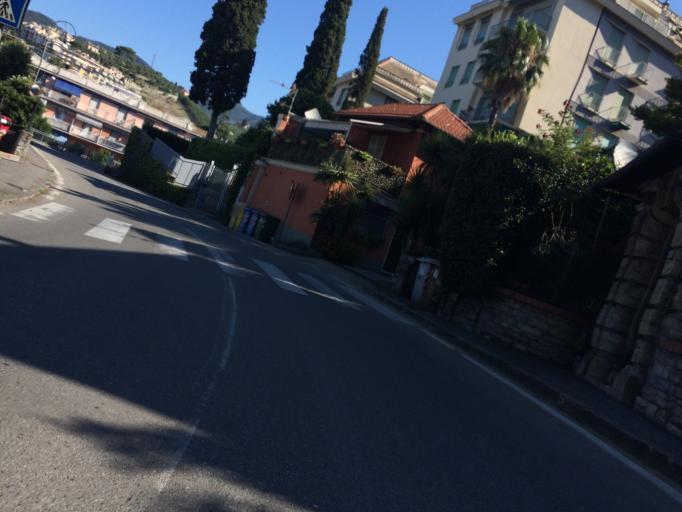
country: IT
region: Liguria
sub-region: Provincia di Genova
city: Rapallo
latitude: 44.3450
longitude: 9.2413
